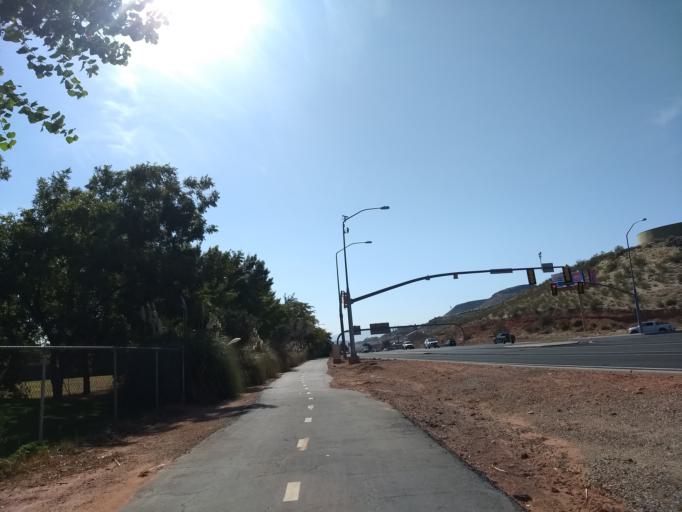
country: US
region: Utah
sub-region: Washington County
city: Saint George
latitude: 37.1251
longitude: -113.6004
